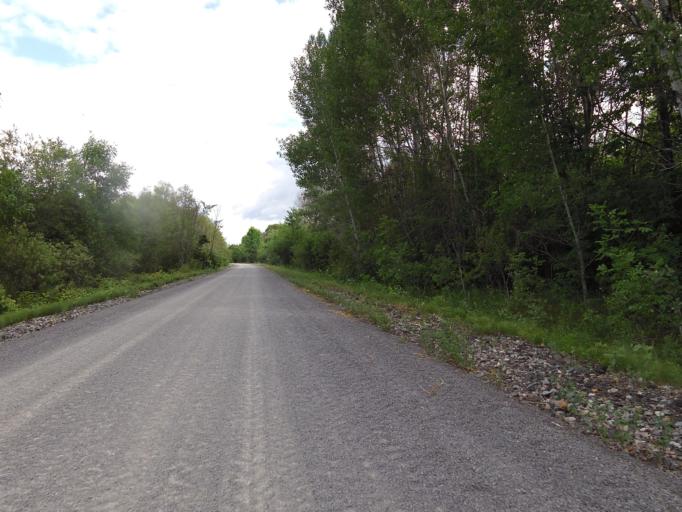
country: CA
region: Ontario
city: Arnprior
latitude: 45.2974
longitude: -76.2626
